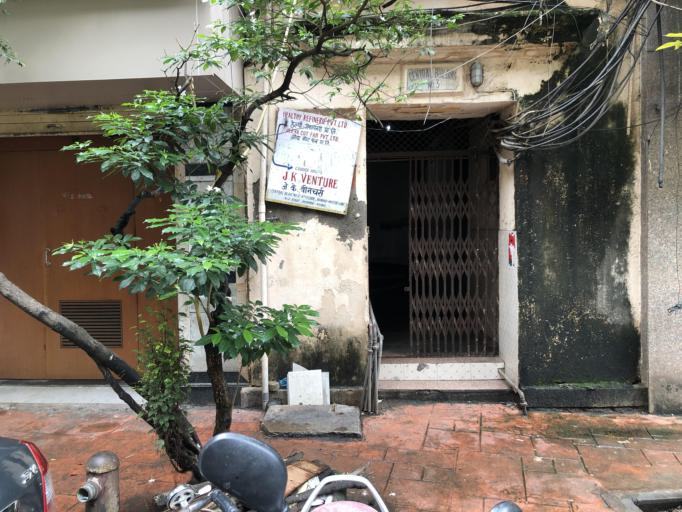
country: IN
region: Maharashtra
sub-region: Raigarh
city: Uran
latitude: 18.9455
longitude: 72.8289
